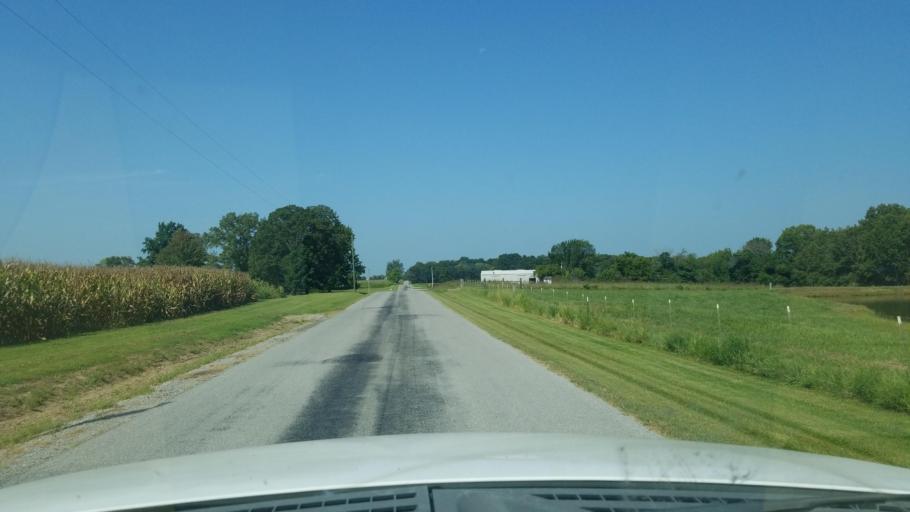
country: US
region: Illinois
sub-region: Saline County
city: Harrisburg
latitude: 37.8925
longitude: -88.6341
